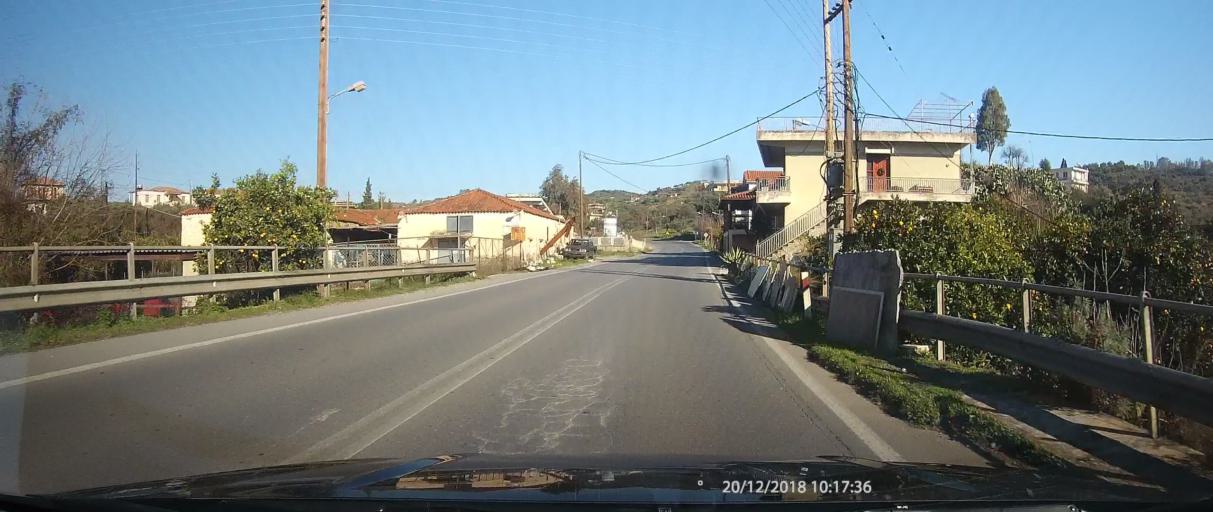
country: GR
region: Peloponnese
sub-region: Nomos Lakonias
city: Sparti
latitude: 37.1085
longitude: 22.4336
